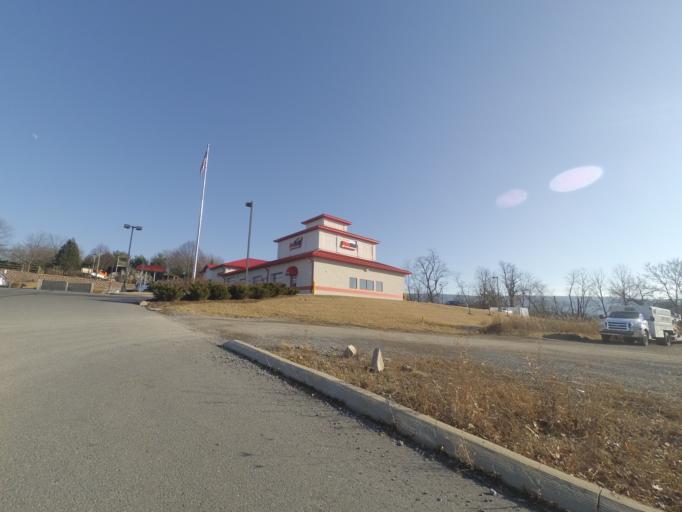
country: US
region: Pennsylvania
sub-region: Centre County
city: State College
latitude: 40.7837
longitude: -77.8316
